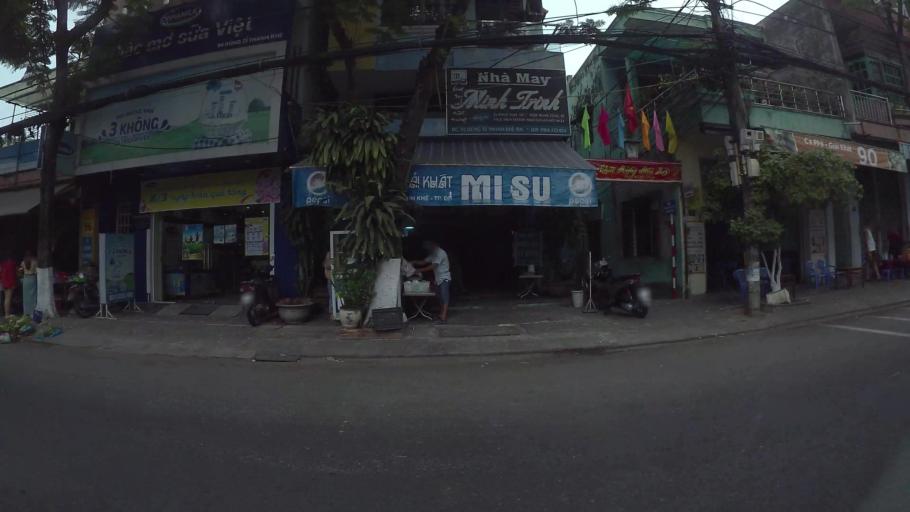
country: VN
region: Da Nang
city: Thanh Khe
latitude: 16.0724
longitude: 108.1784
